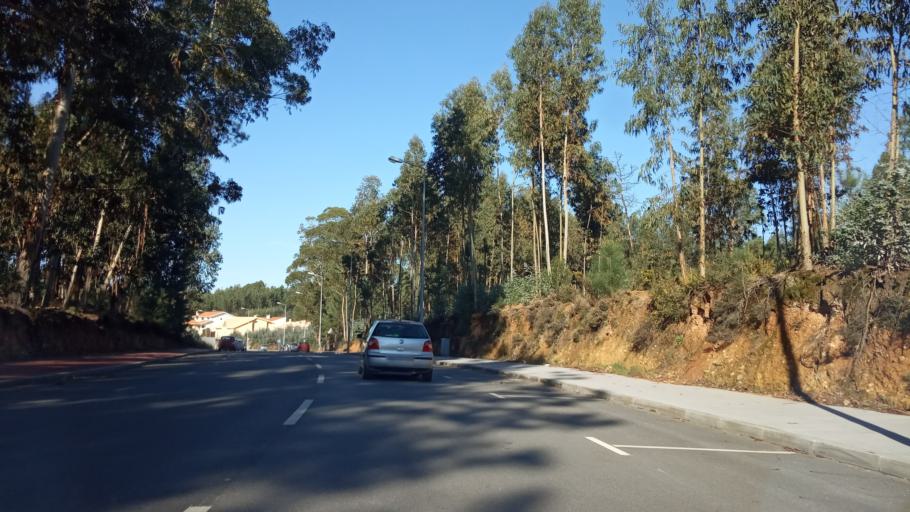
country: PT
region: Aveiro
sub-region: Anadia
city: Anadia
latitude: 40.4301
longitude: -8.4366
